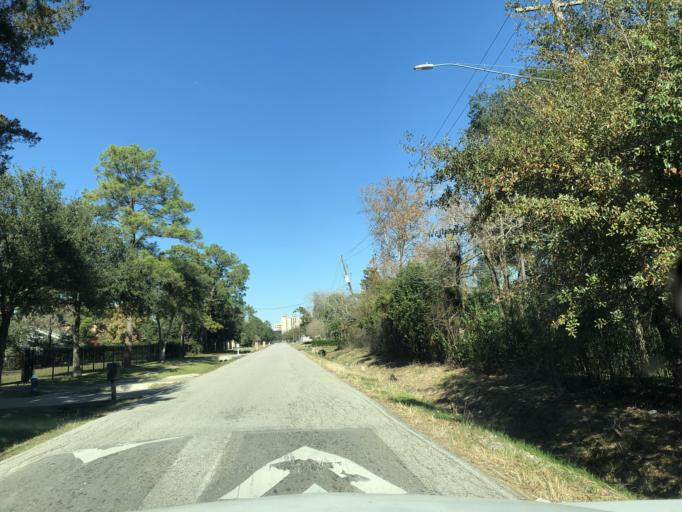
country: US
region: Texas
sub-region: Fort Bend County
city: Missouri City
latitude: 29.6819
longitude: -95.5217
